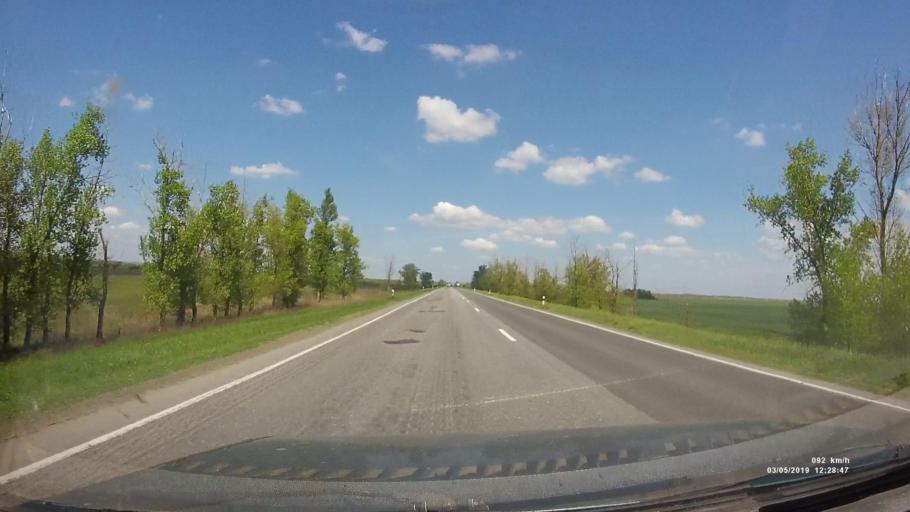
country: RU
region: Rostov
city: Semikarakorsk
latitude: 47.4784
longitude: 40.7308
